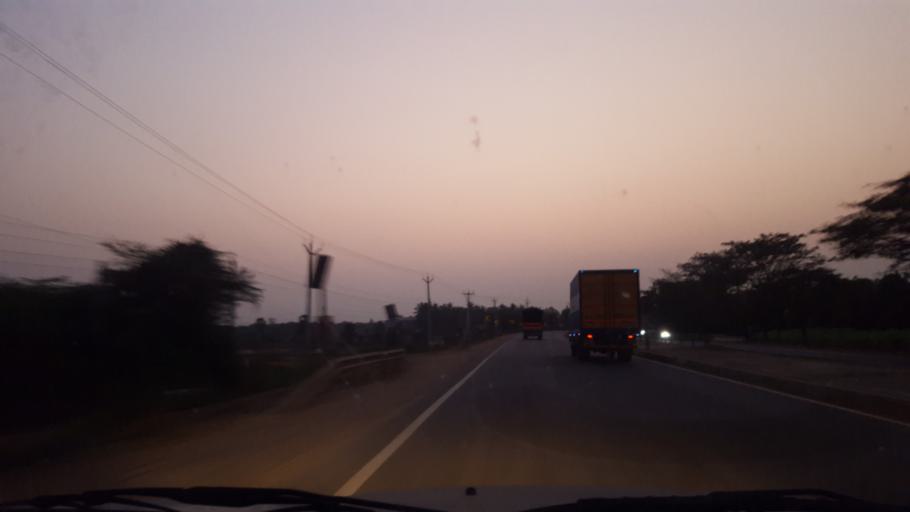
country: IN
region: Andhra Pradesh
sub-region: East Godavari
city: Peddapuram
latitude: 17.1376
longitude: 81.9693
